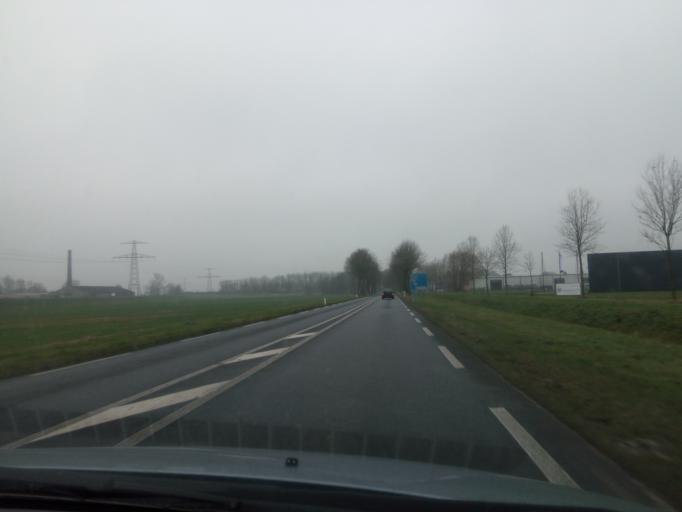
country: NL
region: Groningen
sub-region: Gemeente  Oldambt
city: Winschoten
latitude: 53.1336
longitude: 7.0560
